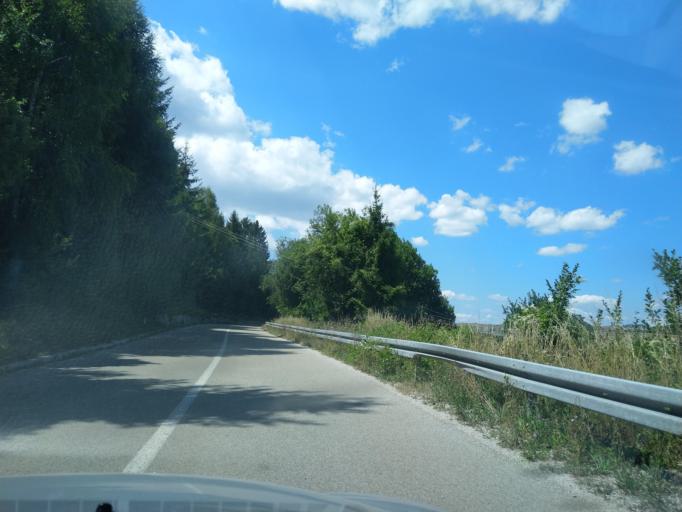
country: RS
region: Central Serbia
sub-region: Zlatiborski Okrug
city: Nova Varos
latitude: 43.3293
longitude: 19.8546
